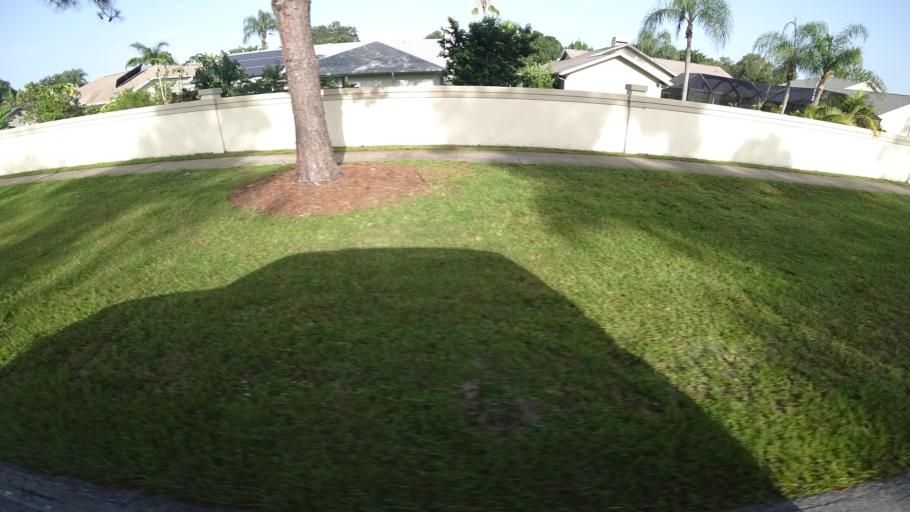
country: US
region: Florida
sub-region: Manatee County
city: Samoset
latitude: 27.4428
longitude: -82.4810
